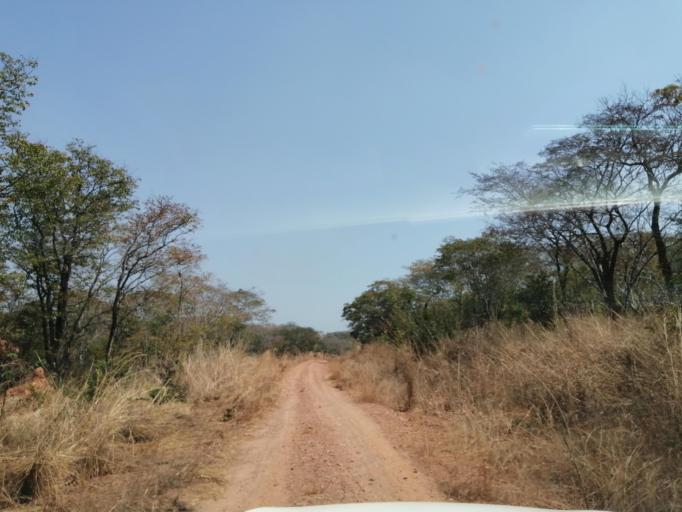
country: ZM
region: Eastern
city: Nyimba
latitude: -14.3229
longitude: 30.0427
